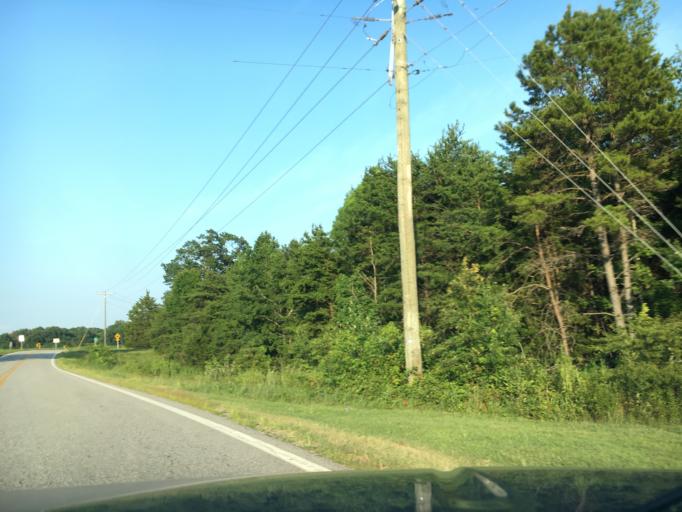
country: US
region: Virginia
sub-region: Halifax County
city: Mountain Road
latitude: 36.8330
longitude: -79.1491
